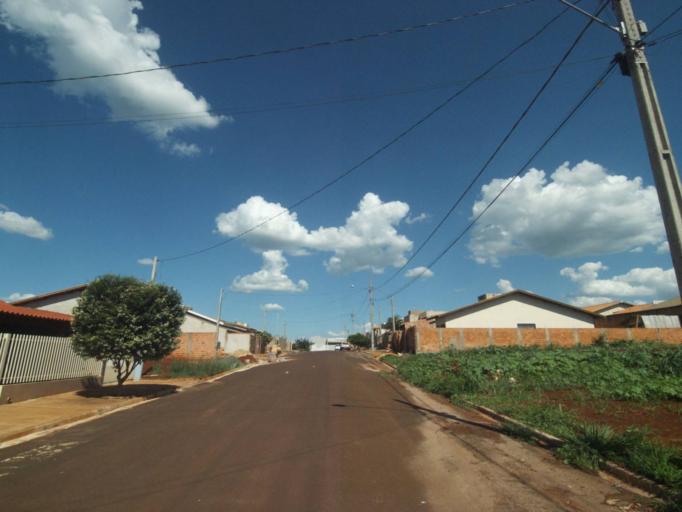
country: BR
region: Parana
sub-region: Sertanopolis
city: Sertanopolis
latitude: -23.0366
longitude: -50.8112
